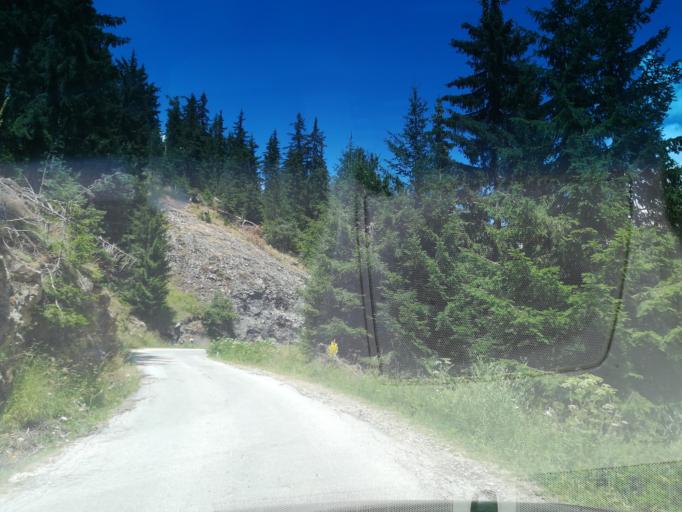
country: BG
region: Smolyan
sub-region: Obshtina Chepelare
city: Chepelare
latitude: 41.6844
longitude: 24.7697
